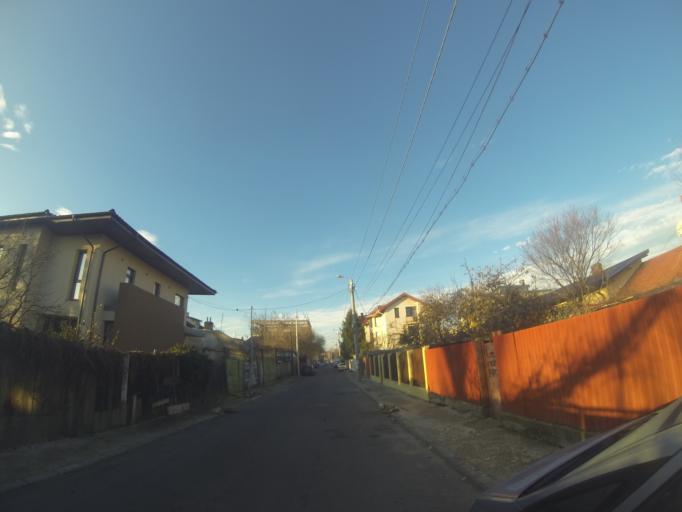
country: RO
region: Bucuresti
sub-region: Municipiul Bucuresti
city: Bucuresti
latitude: 44.4076
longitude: 26.0837
